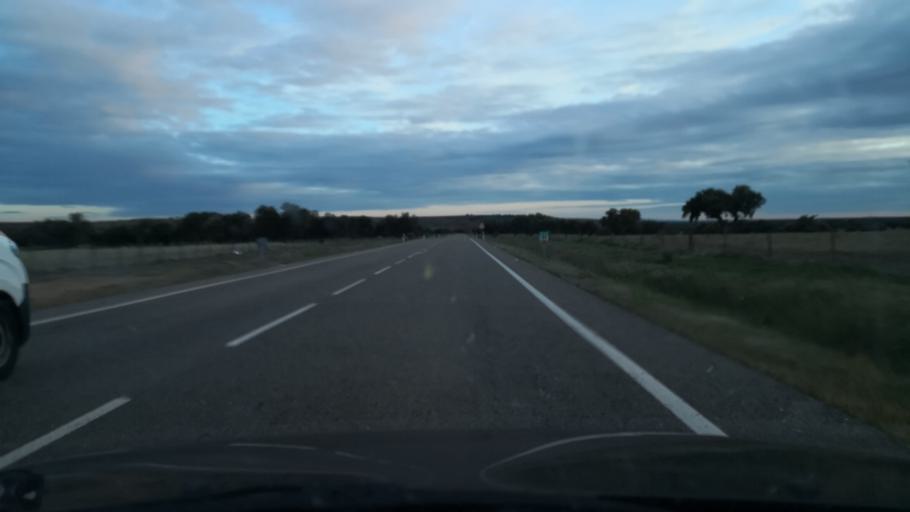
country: ES
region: Extremadura
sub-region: Provincia de Badajoz
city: La Roca de la Sierra
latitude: 39.1052
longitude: -6.7100
